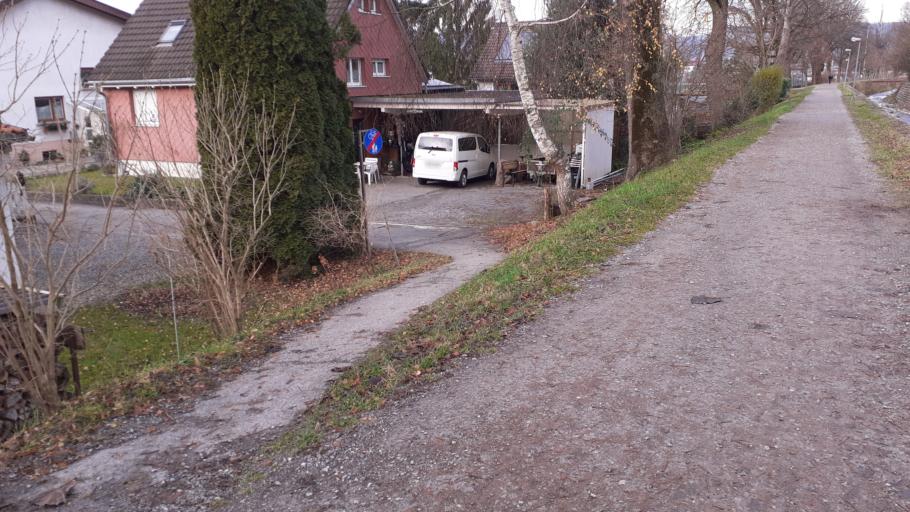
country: AT
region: Vorarlberg
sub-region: Politischer Bezirk Dornbirn
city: Hohenems
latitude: 47.3680
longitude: 9.6830
